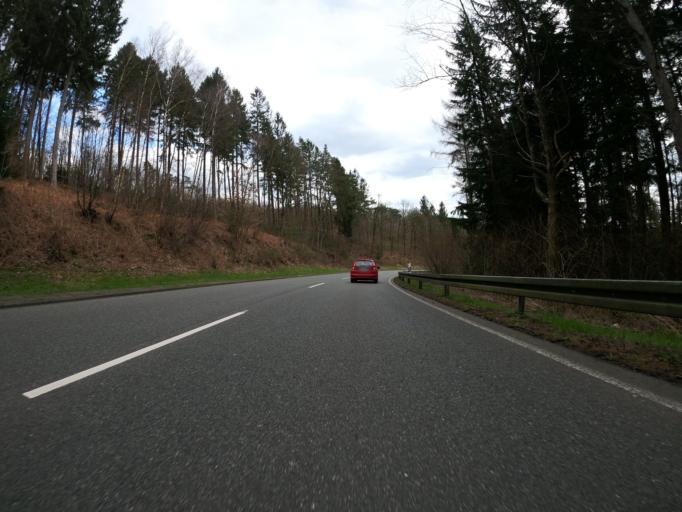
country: DE
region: North Rhine-Westphalia
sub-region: Regierungsbezirk Dusseldorf
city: Solingen
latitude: 51.1974
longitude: 7.1141
